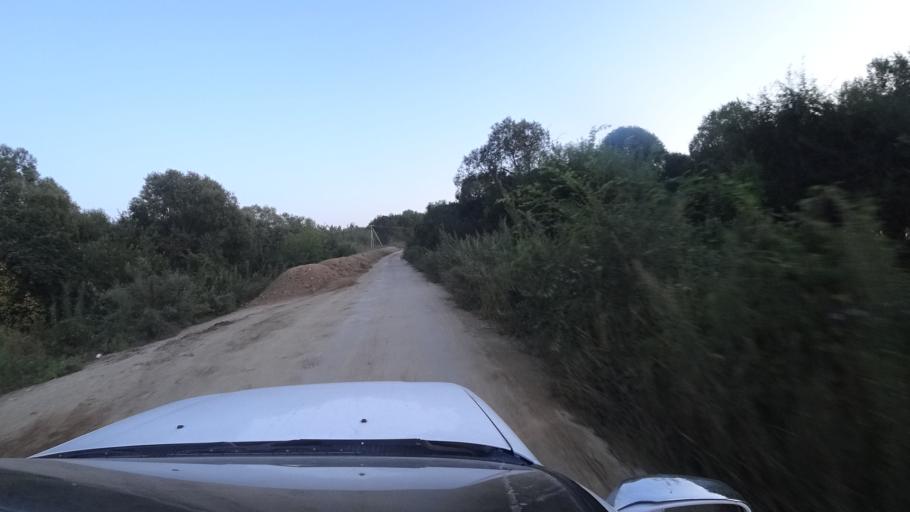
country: RU
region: Primorskiy
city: Dal'nerechensk
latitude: 45.9381
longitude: 133.7601
